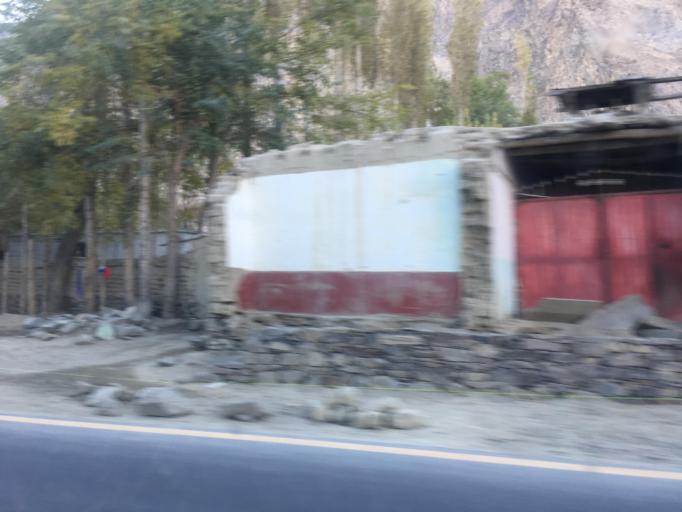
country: PK
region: Gilgit-Baltistan
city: Skardu
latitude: 35.3594
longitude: 75.5083
